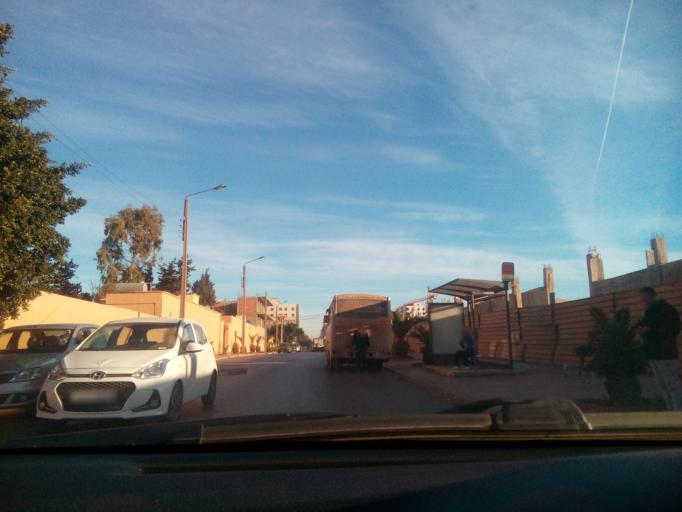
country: DZ
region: Oran
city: Oran
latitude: 35.6763
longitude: -0.6619
